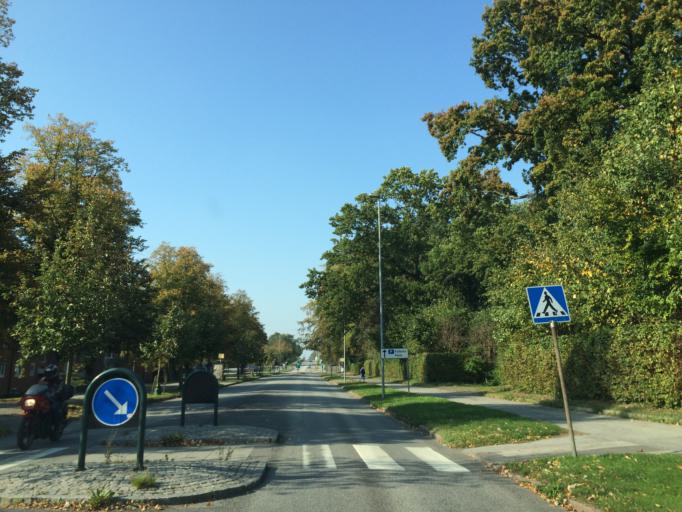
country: SE
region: Skane
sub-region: Lunds Kommun
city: Lund
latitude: 55.7030
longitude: 13.1686
